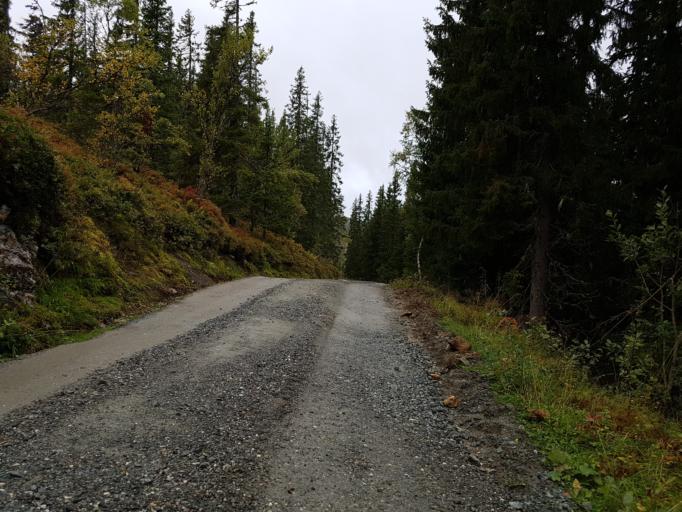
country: NO
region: Sor-Trondelag
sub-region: Melhus
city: Melhus
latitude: 63.4133
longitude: 10.2504
